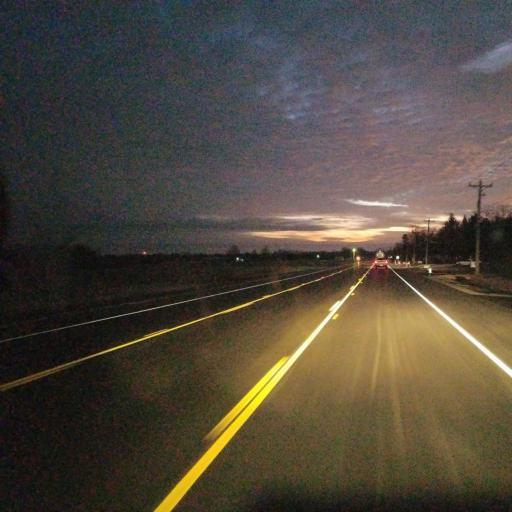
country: US
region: Illinois
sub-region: Peoria County
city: Hanna City
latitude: 40.6917
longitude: -89.7853
